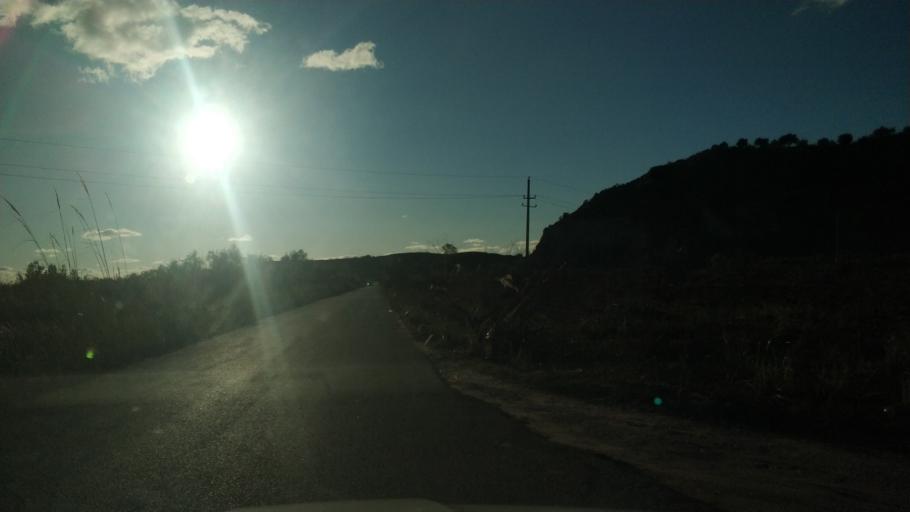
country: AL
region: Vlore
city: Vlore
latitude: 40.5053
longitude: 19.4228
